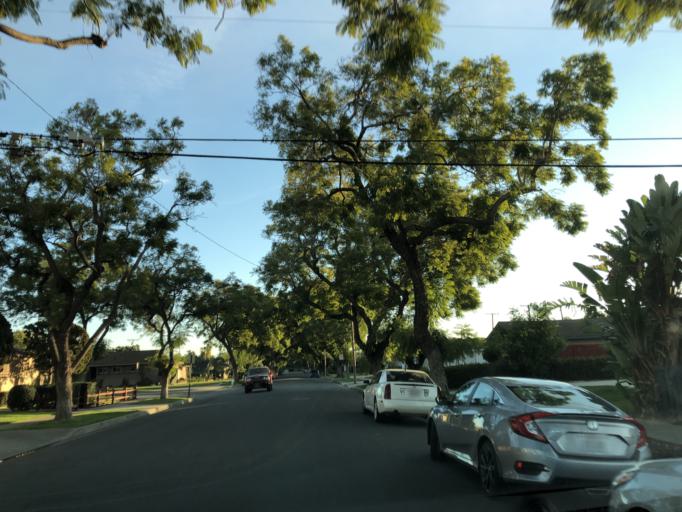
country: US
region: California
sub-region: Orange County
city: Santa Ana
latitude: 33.7571
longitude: -117.8488
